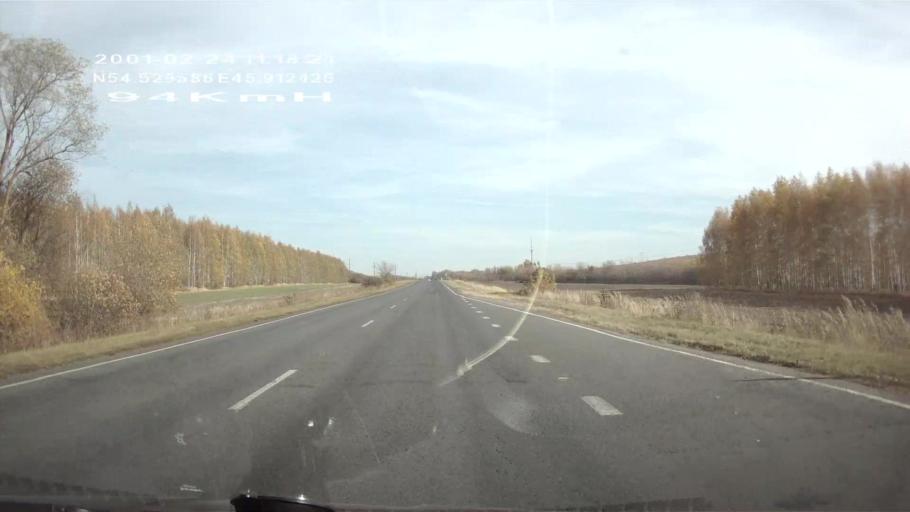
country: RU
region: Mordoviya
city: Atyashevo
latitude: 54.5294
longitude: 45.9121
